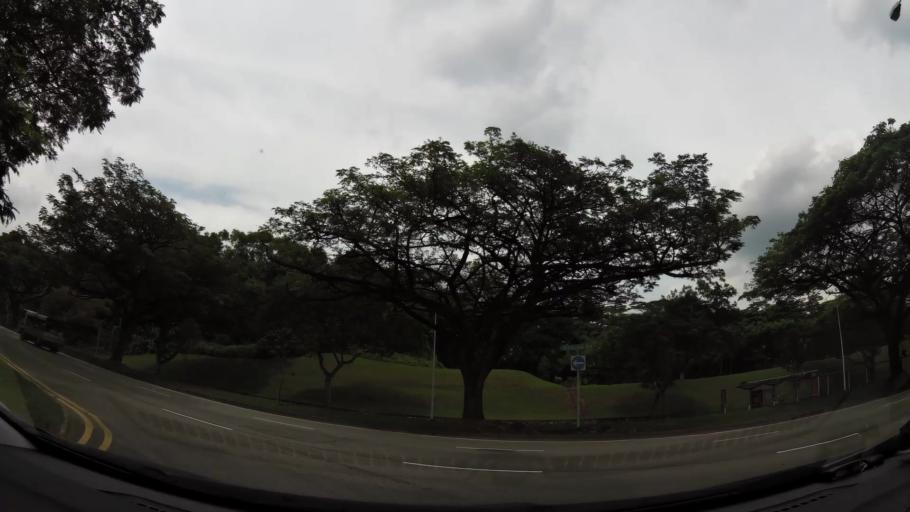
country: SG
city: Singapore
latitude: 1.3195
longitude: 103.7821
